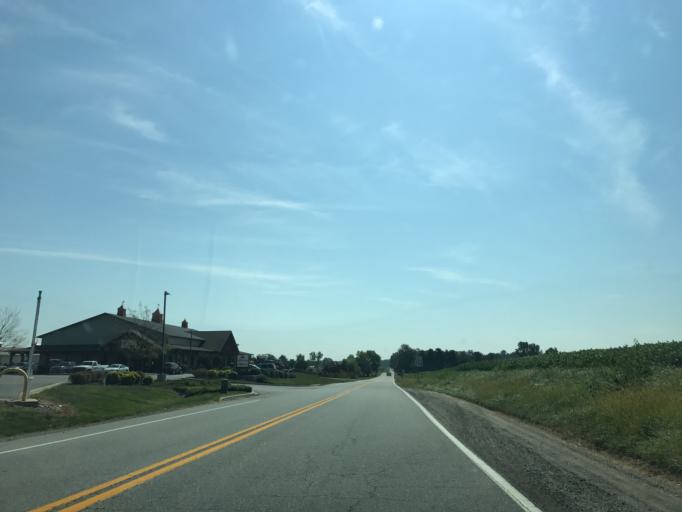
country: US
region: Maryland
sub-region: Queen Anne's County
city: Kingstown
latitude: 39.3201
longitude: -75.9770
